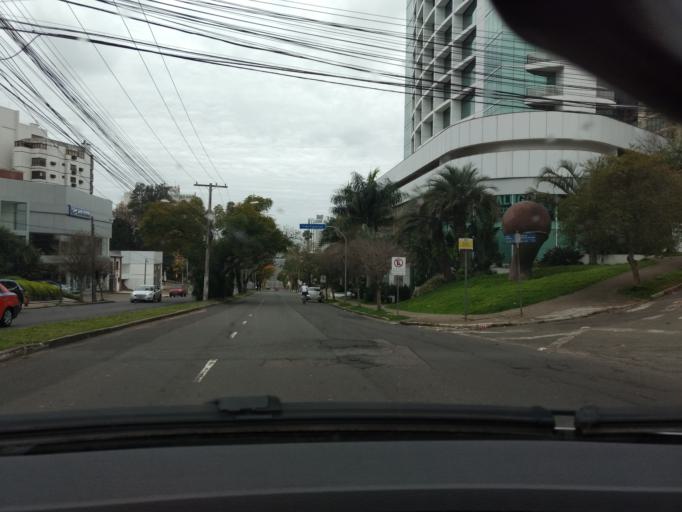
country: BR
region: Rio Grande do Sul
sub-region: Porto Alegre
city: Porto Alegre
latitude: -30.0294
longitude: -51.1803
